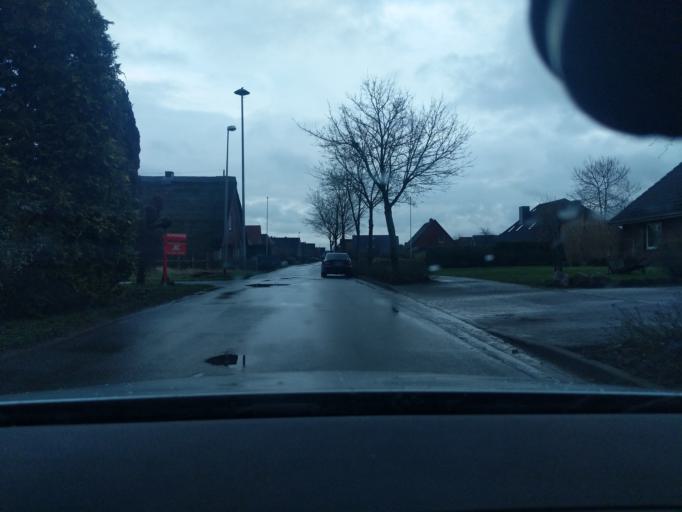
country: DE
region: Lower Saxony
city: Jork
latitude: 53.5231
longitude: 9.6518
